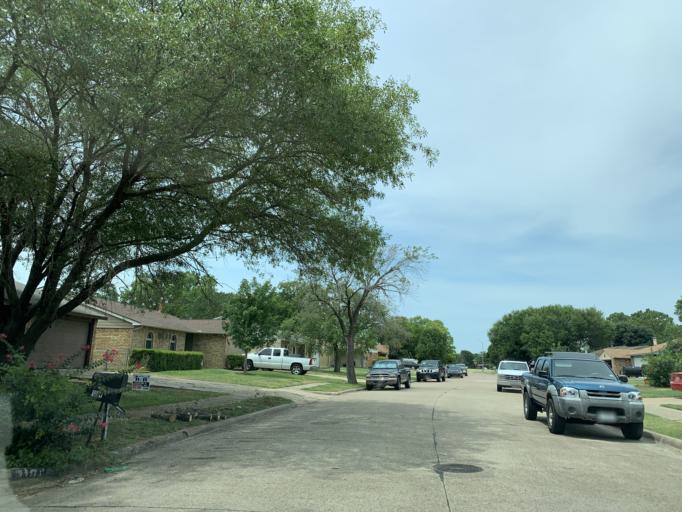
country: US
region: Texas
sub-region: Dallas County
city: Cedar Hill
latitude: 32.6550
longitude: -97.0192
